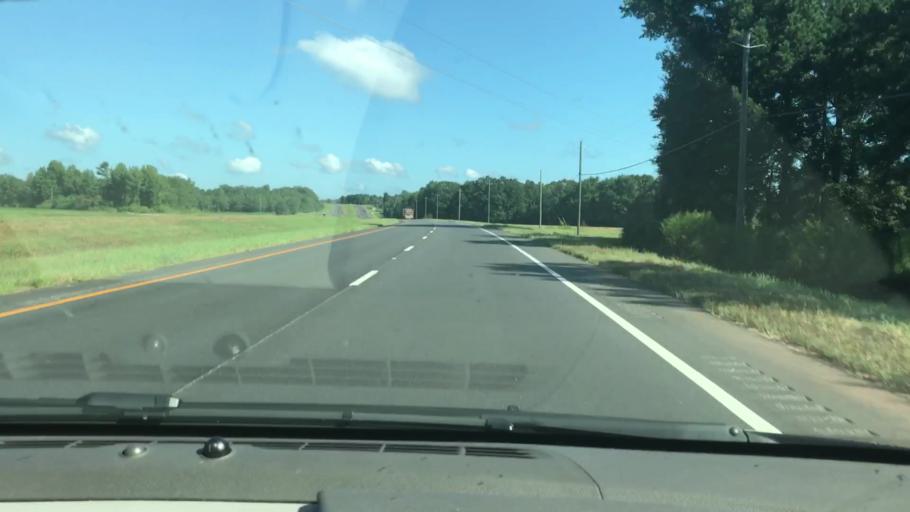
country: US
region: Alabama
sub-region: Barbour County
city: Eufaula
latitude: 32.0181
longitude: -85.1174
